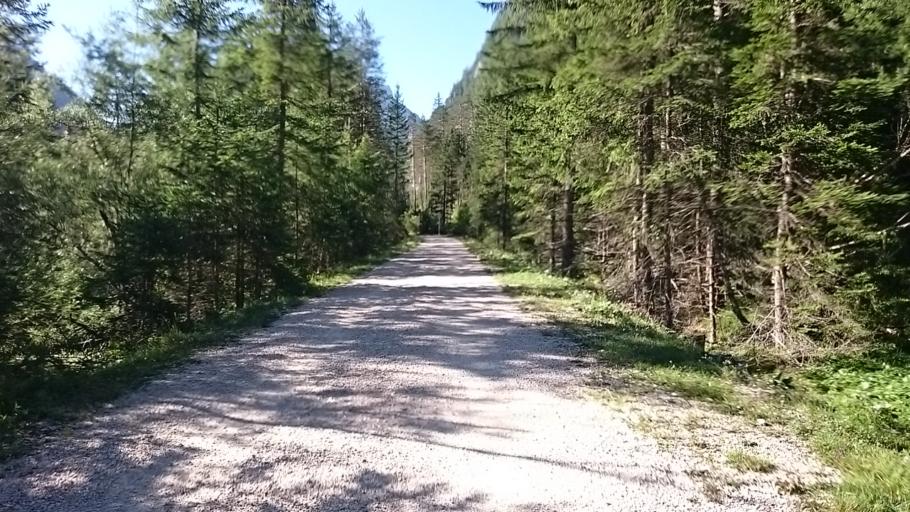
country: IT
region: Trentino-Alto Adige
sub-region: Bolzano
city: Dobbiaco
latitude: 46.6522
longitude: 12.2272
